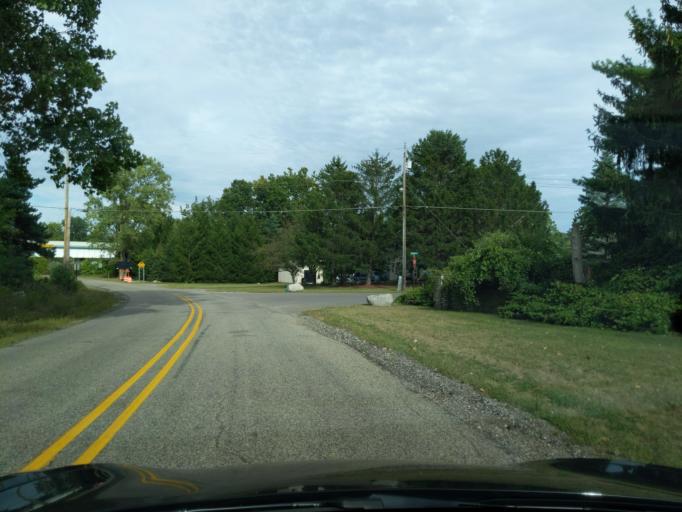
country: US
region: Michigan
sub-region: Eaton County
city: Dimondale
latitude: 42.6692
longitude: -84.6474
